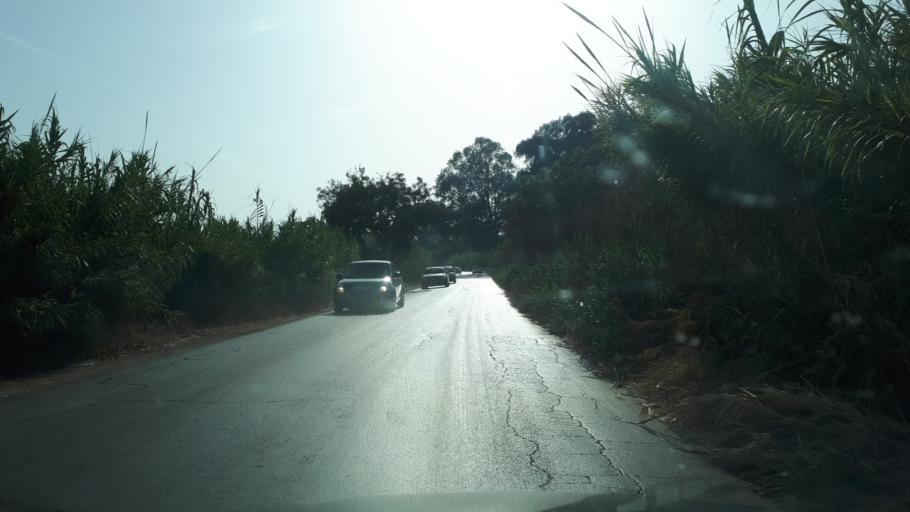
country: DZ
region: Tipaza
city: Cheraga
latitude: 36.7357
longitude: 2.9102
